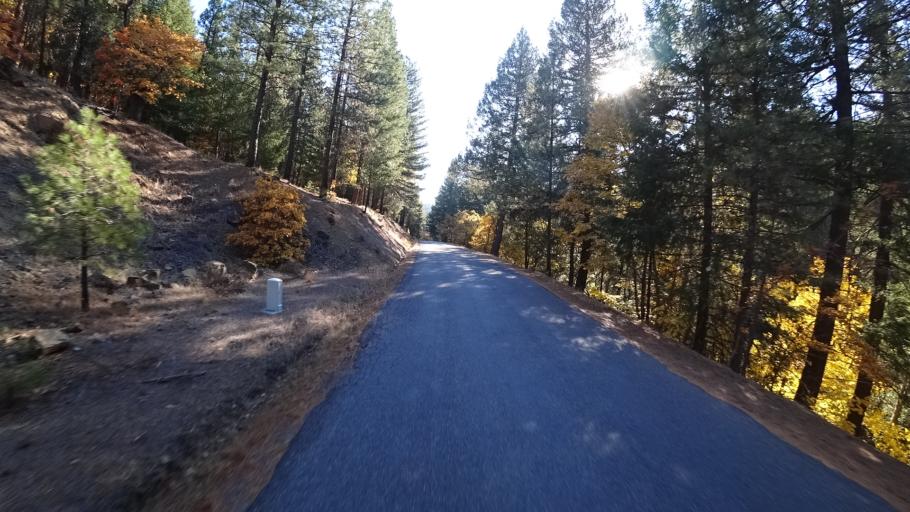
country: US
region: California
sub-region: Siskiyou County
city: Yreka
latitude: 41.6409
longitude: -123.0147
